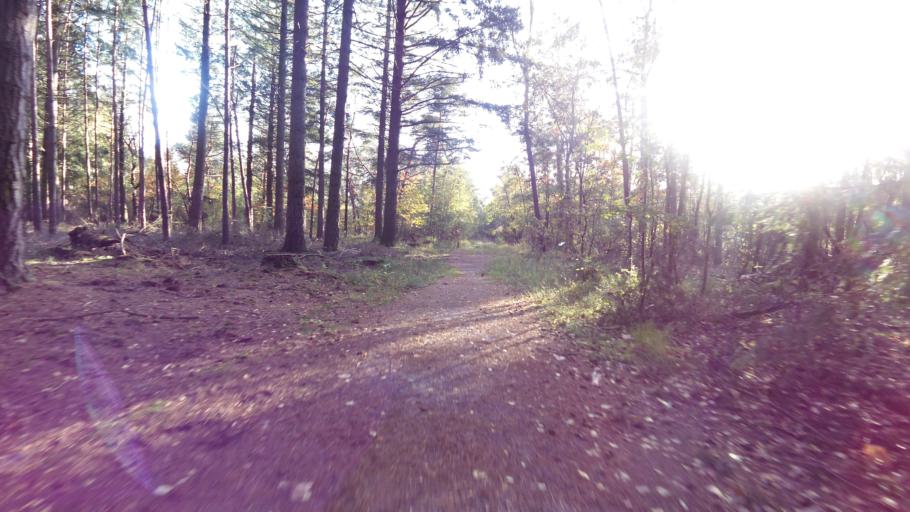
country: NL
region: Gelderland
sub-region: Gemeente Heerde
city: Heerde
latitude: 52.3936
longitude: 5.9945
